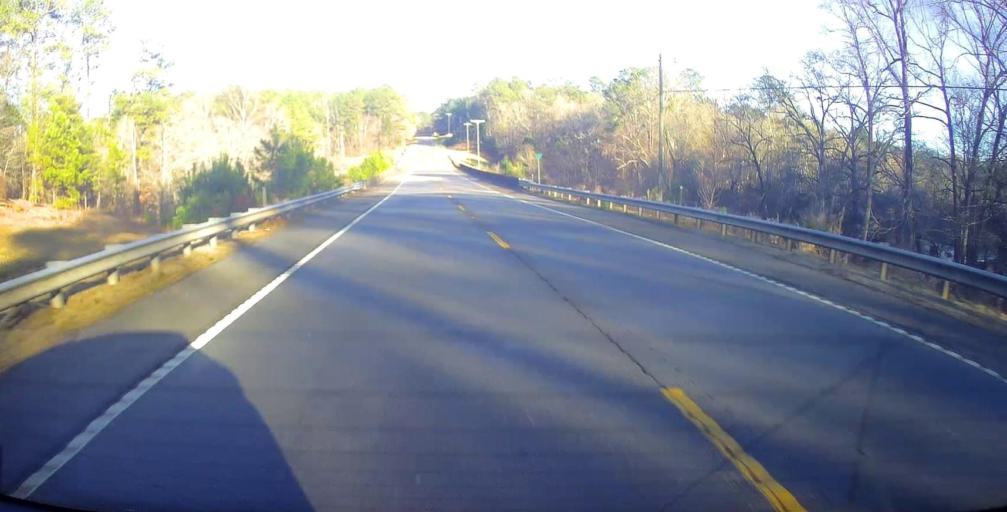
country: US
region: Georgia
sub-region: Upson County
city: Thomaston
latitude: 32.8788
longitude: -84.3766
